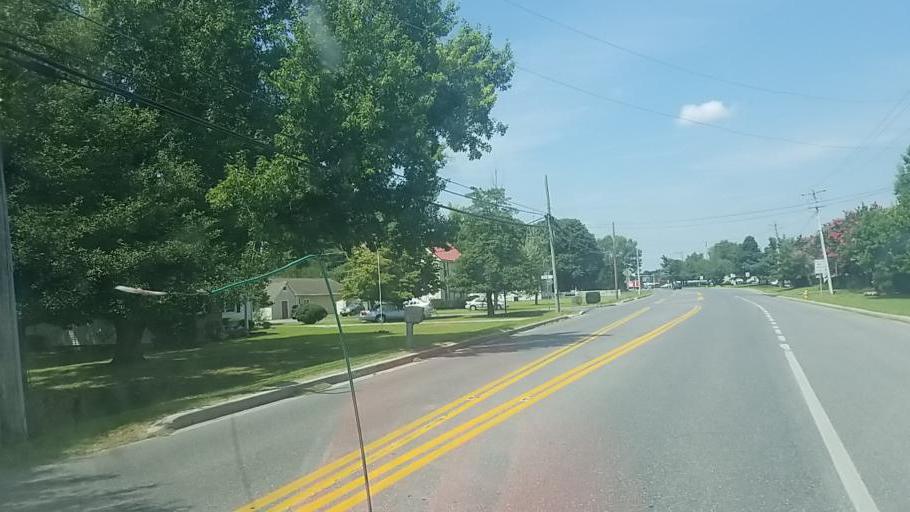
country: US
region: Maryland
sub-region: Wicomico County
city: Salisbury
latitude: 38.3653
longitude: -75.5633
